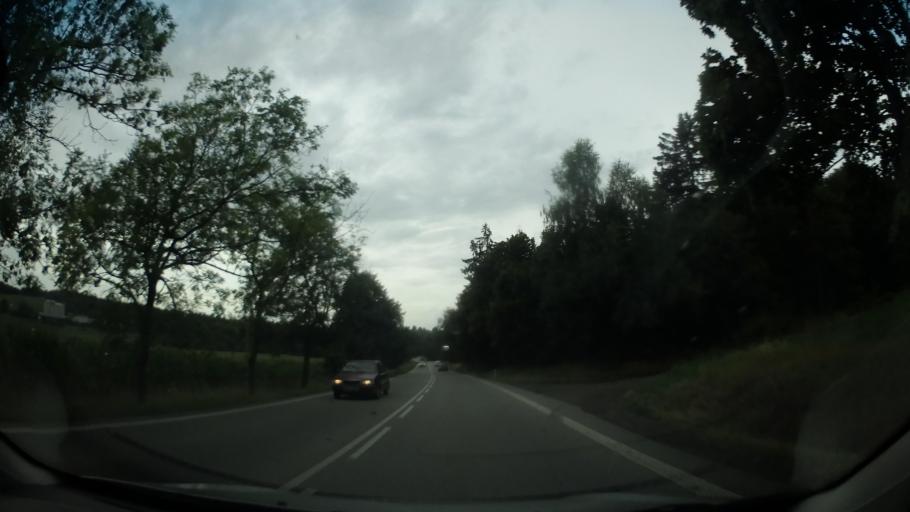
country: CZ
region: Vysocina
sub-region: Okres Zd'ar nad Sazavou
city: Zd'ar nad Sazavou
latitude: 49.5617
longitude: 16.0045
